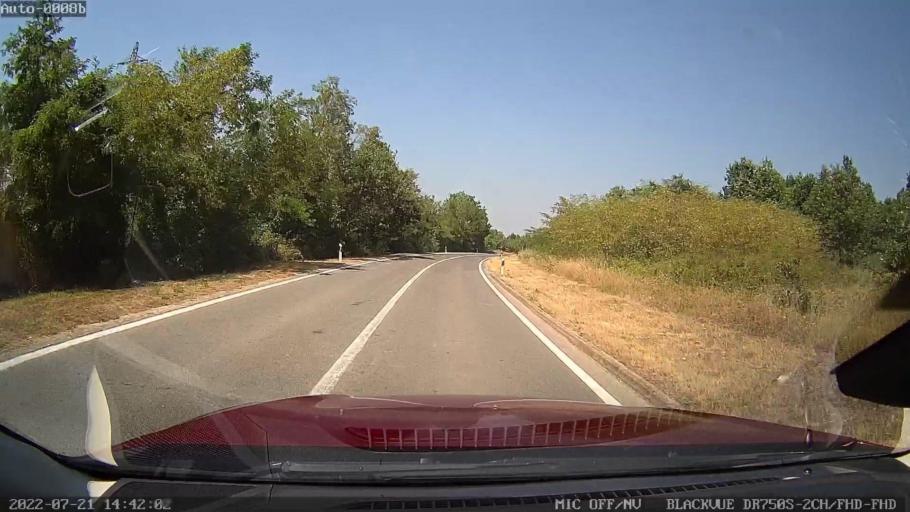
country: HR
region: Istarska
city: Vodnjan
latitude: 45.0945
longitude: 13.8807
